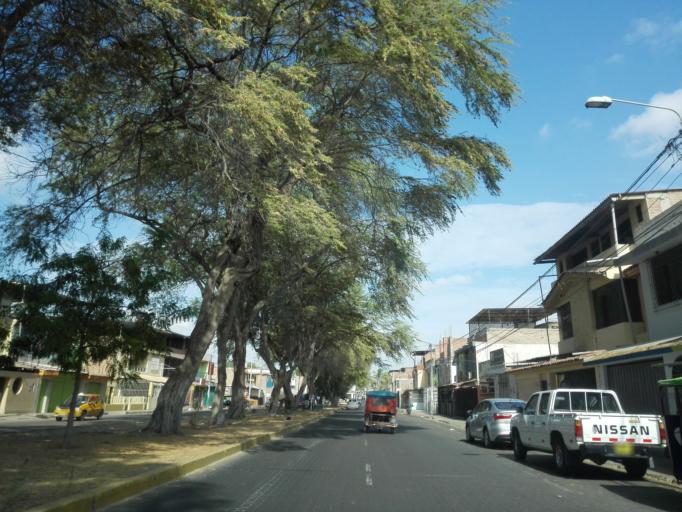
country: PE
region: Piura
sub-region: Provincia de Piura
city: Piura
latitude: -5.1904
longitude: -80.6461
